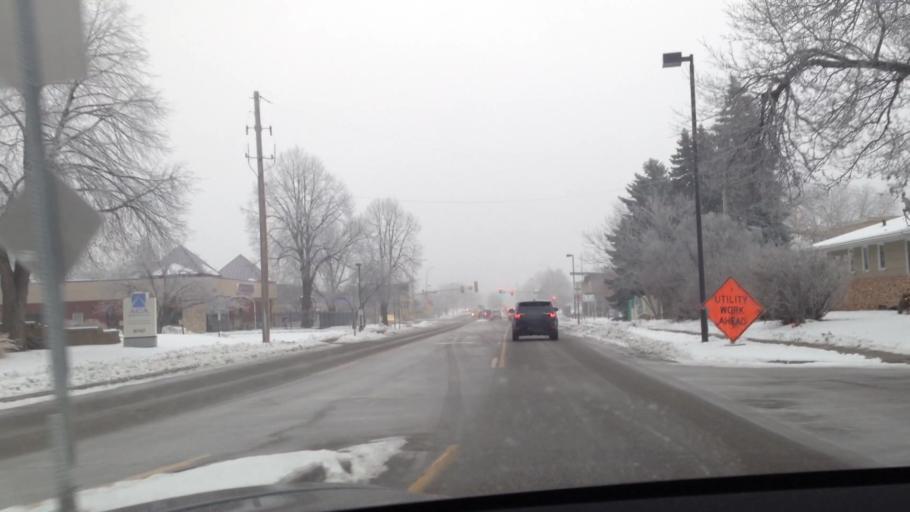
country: US
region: Minnesota
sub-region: Hennepin County
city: Edina
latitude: 44.8764
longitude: -93.3316
